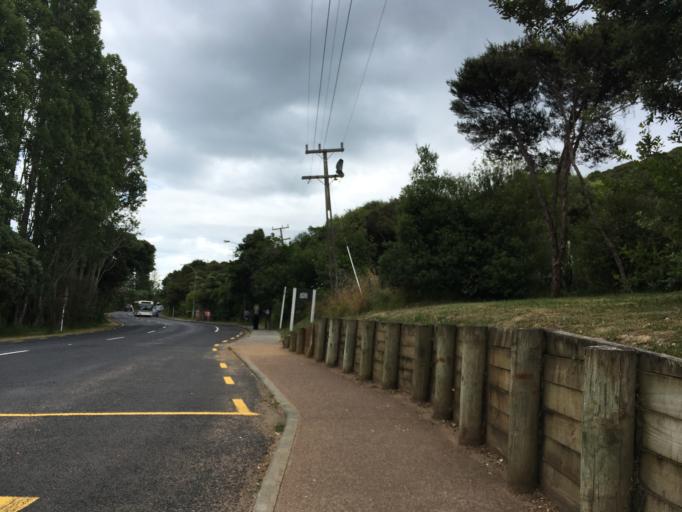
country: NZ
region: Auckland
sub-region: Auckland
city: Pakuranga
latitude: -36.7814
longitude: 174.9991
